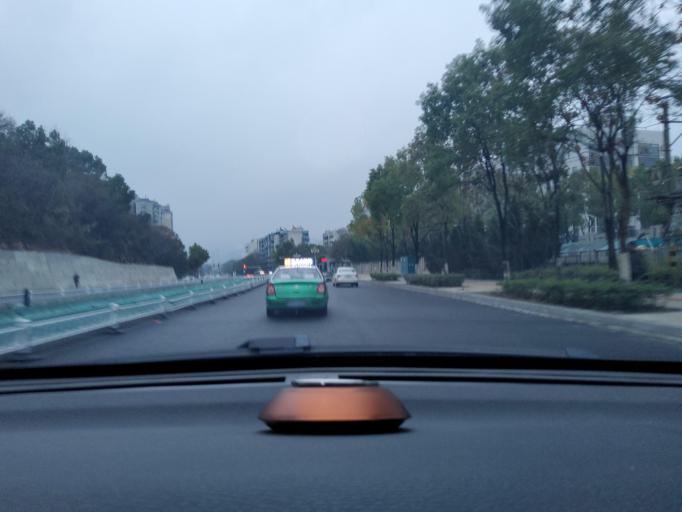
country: CN
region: Hubei
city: Tuanchengshan
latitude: 30.1933
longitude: 115.0250
